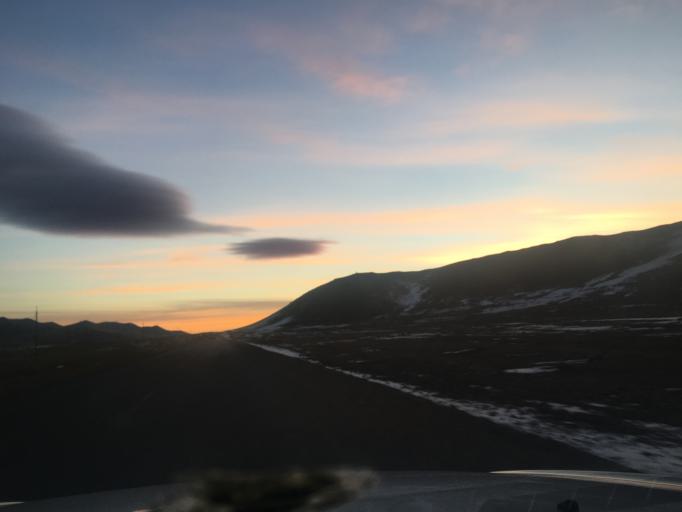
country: MN
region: Central Aimak
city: Mandal
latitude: 48.1151
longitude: 106.6422
